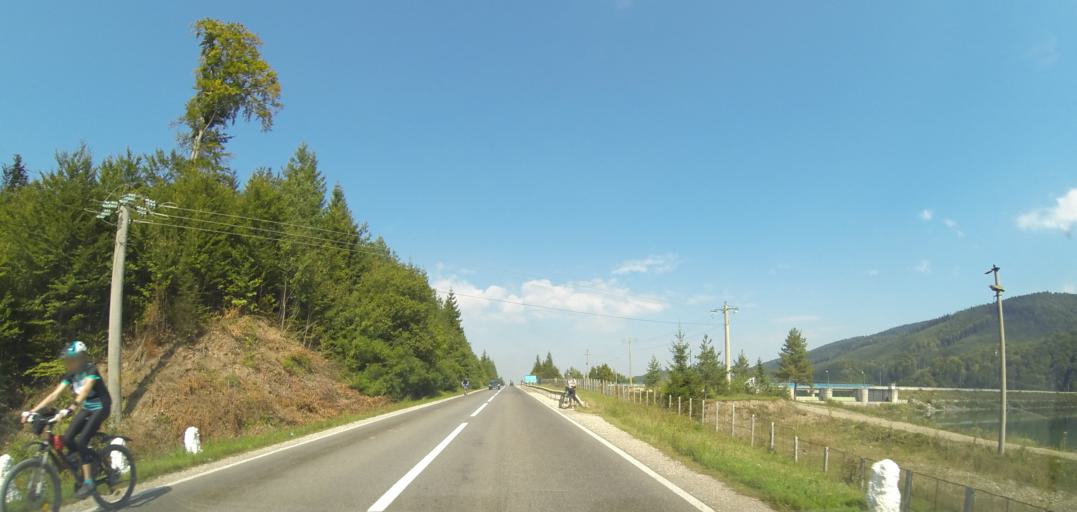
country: RO
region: Brasov
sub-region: Comuna Tarlungeni
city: Tarlungeni
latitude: 45.5792
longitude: 25.7609
